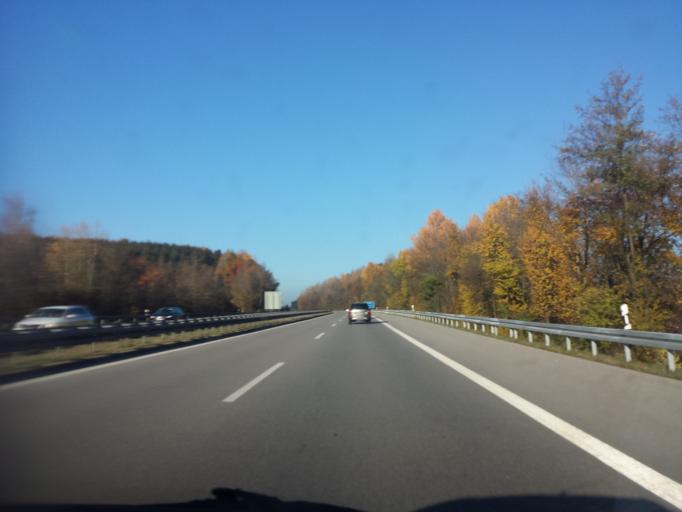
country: DE
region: Bavaria
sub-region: Upper Bavaria
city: Sindelsdorf
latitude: 47.7316
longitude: 11.3276
